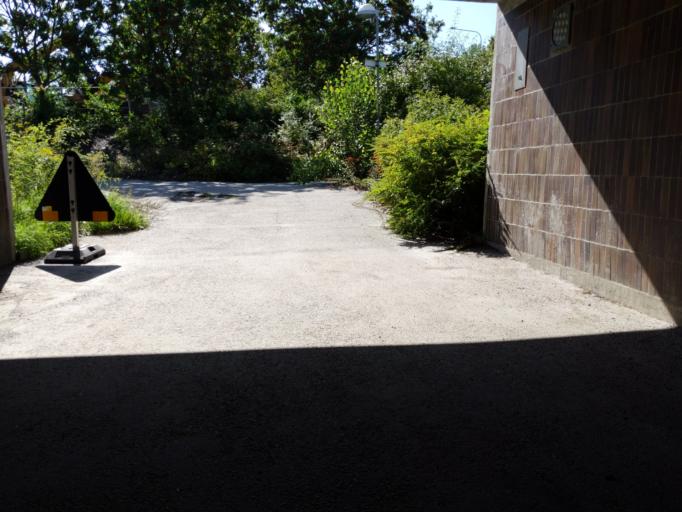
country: SE
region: Stockholm
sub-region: Sundbybergs Kommun
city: Sundbyberg
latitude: 59.3773
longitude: 17.9660
